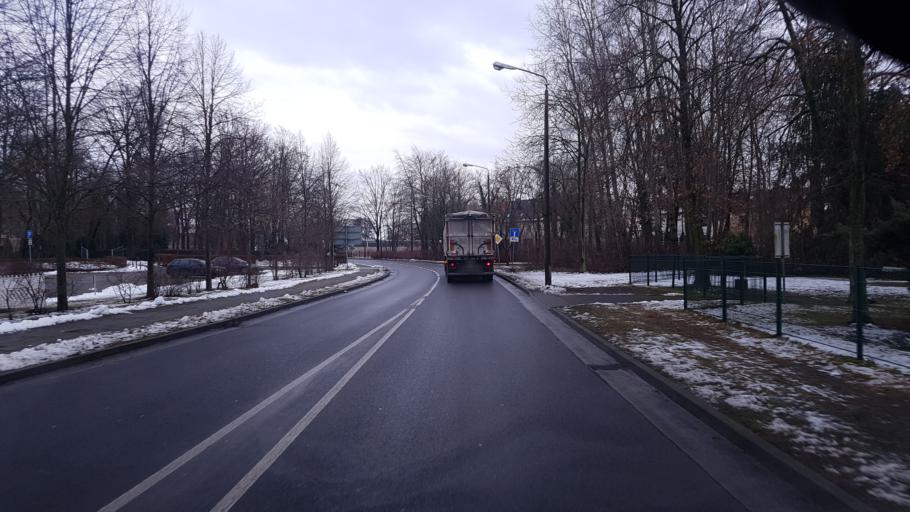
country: DE
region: Brandenburg
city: Peitz
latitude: 51.8523
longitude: 14.4083
